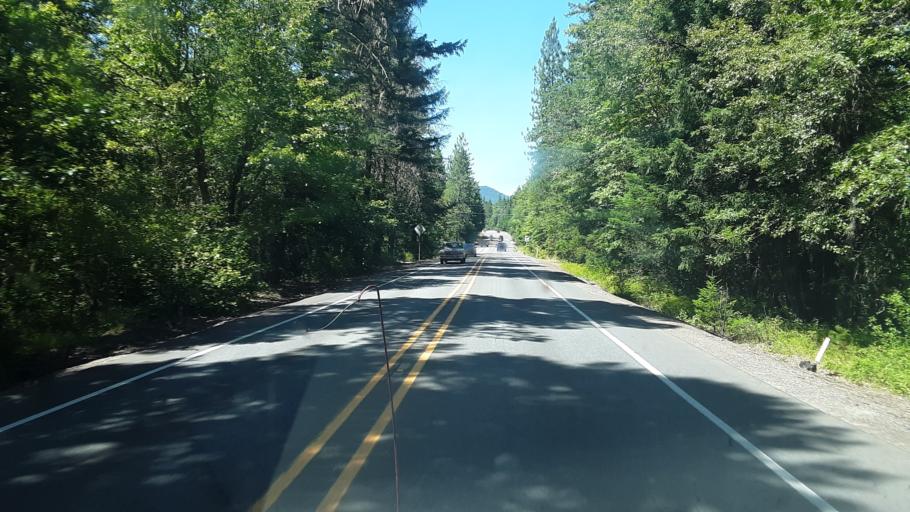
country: US
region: Oregon
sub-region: Josephine County
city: Cave Junction
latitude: 42.2579
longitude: -123.6188
